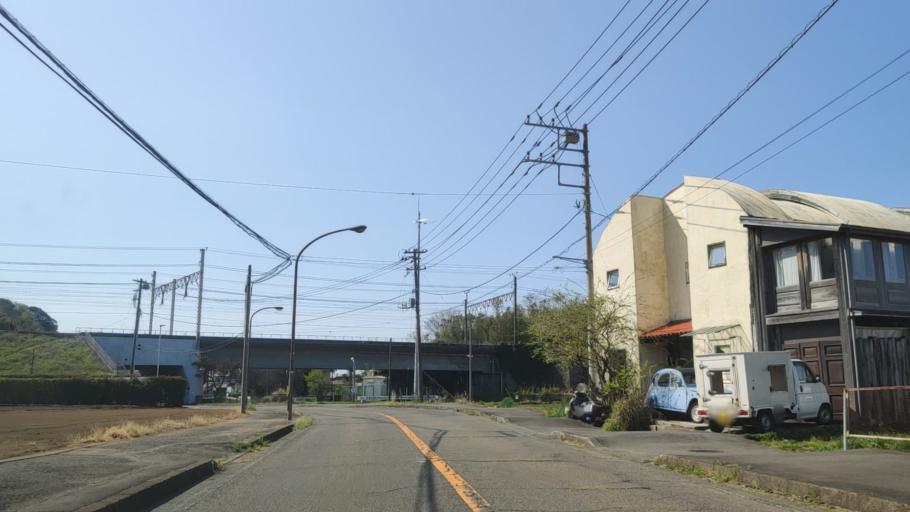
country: JP
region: Kanagawa
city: Oiso
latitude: 35.3078
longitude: 139.2884
